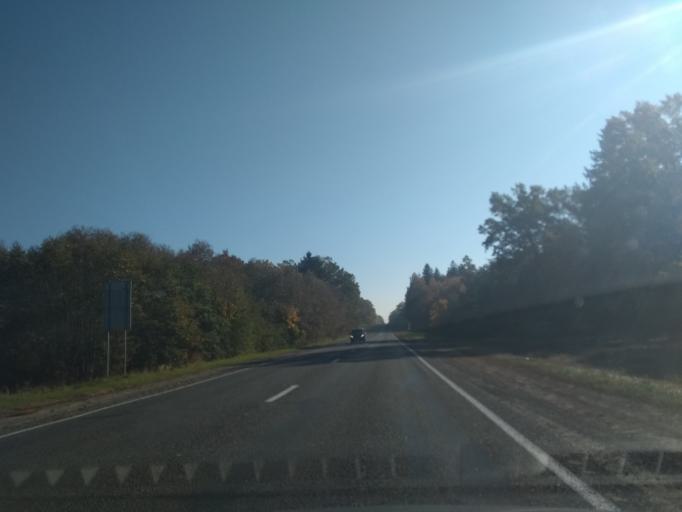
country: BY
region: Grodnenskaya
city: Slonim
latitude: 53.1116
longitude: 25.1640
